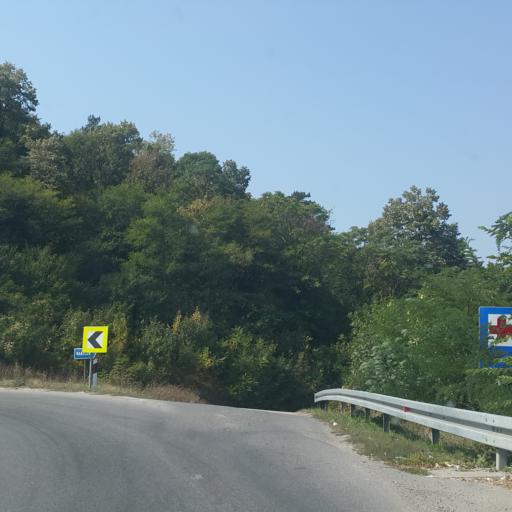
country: RS
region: Central Serbia
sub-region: Zajecarski Okrug
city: Zajecar
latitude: 43.8962
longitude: 22.2880
